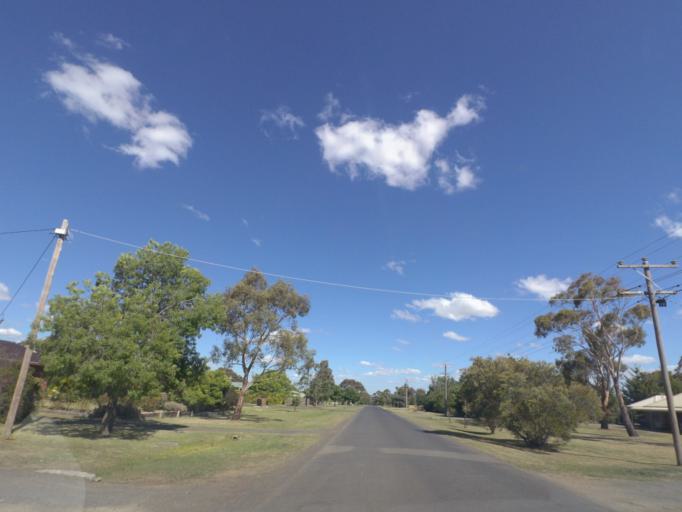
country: AU
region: Victoria
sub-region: Hume
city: Sunbury
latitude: -37.4614
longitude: 144.6700
